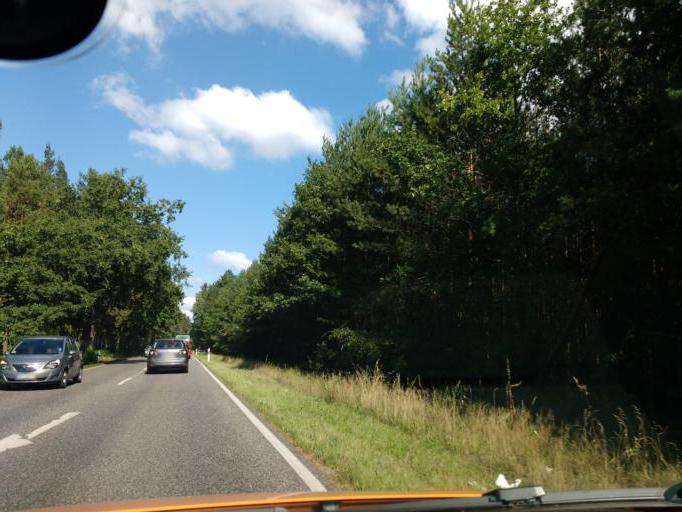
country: DE
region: Brandenburg
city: Birkenwerder
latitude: 52.7207
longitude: 13.2676
